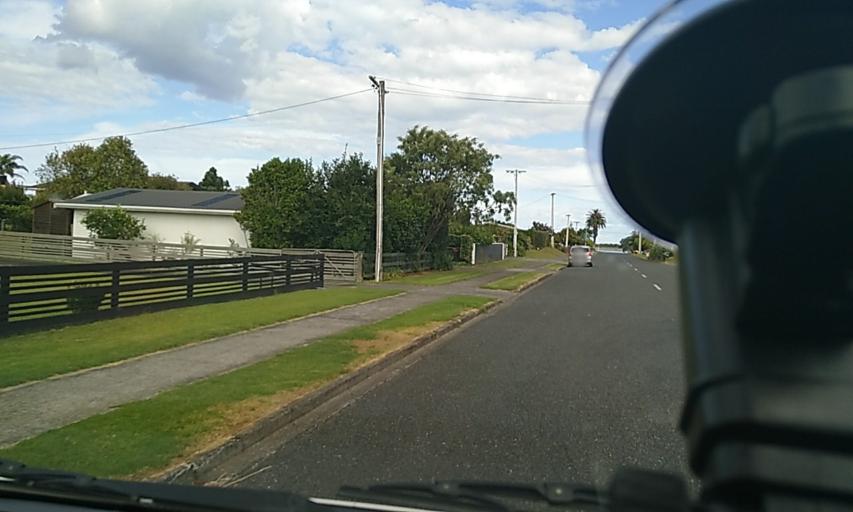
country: NZ
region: Bay of Plenty
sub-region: Western Bay of Plenty District
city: Waihi Beach
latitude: -37.4462
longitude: 175.9643
